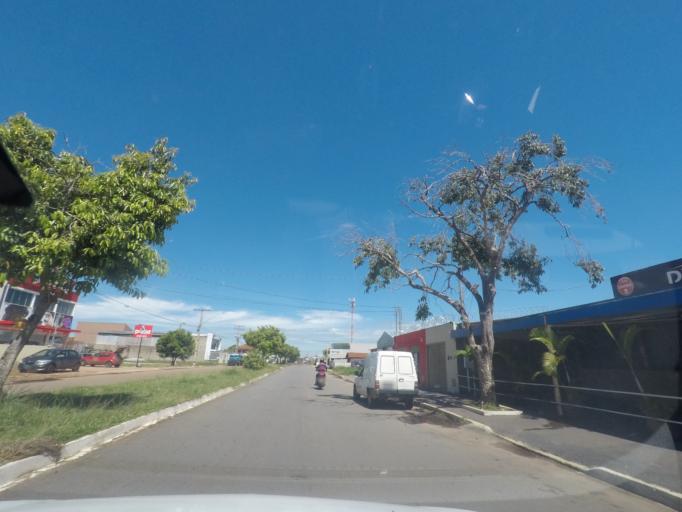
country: BR
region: Goias
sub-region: Aparecida De Goiania
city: Aparecida de Goiania
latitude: -16.7687
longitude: -49.3465
